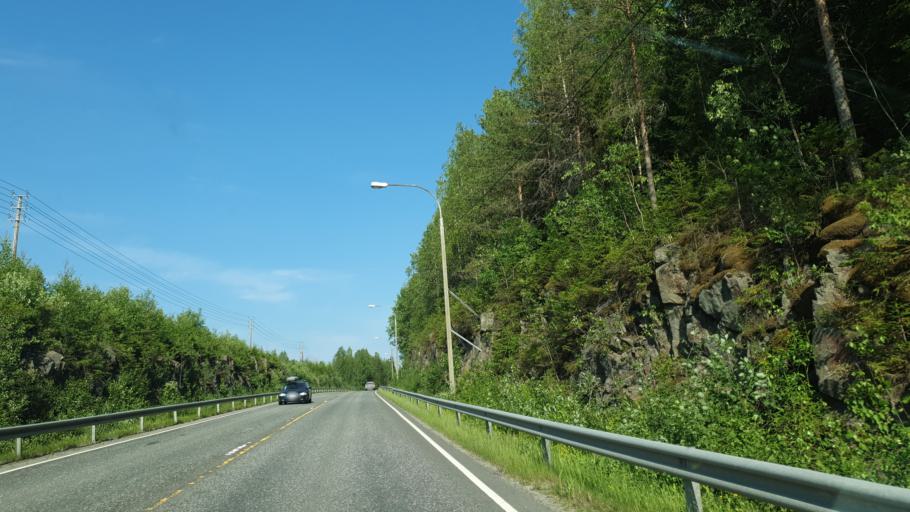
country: FI
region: Northern Savo
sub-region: Kuopio
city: Siilinjaervi
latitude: 63.1359
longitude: 27.8297
